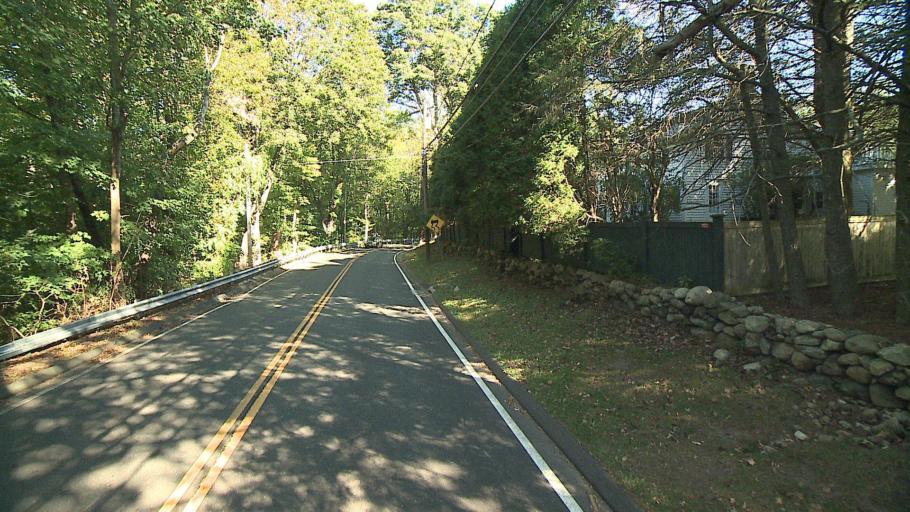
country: US
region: Connecticut
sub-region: Fairfield County
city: Darien
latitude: 41.1099
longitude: -73.4856
